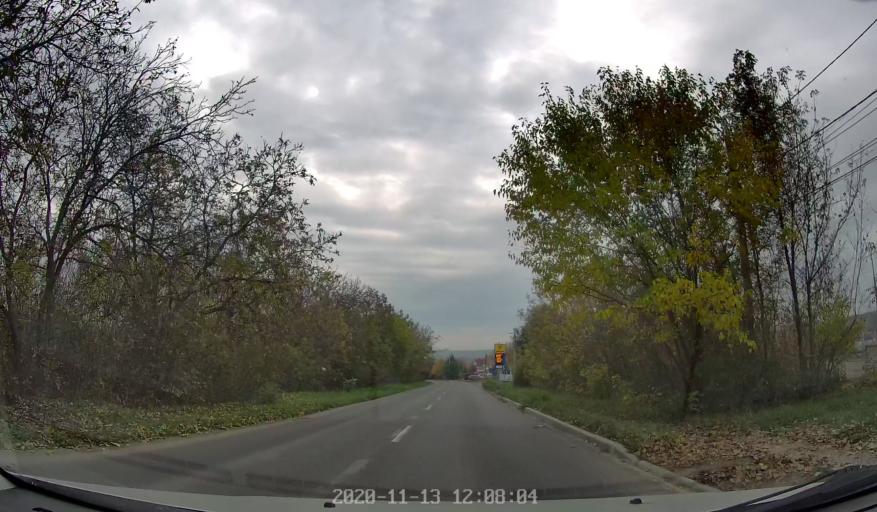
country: MD
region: Chisinau
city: Chisinau
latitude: 46.9691
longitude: 28.8335
